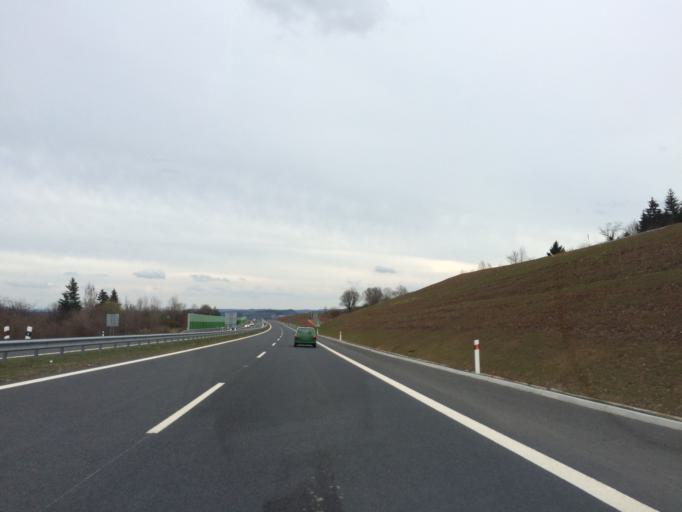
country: CZ
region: Ustecky
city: Lubenec
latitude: 50.1333
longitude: 13.2629
